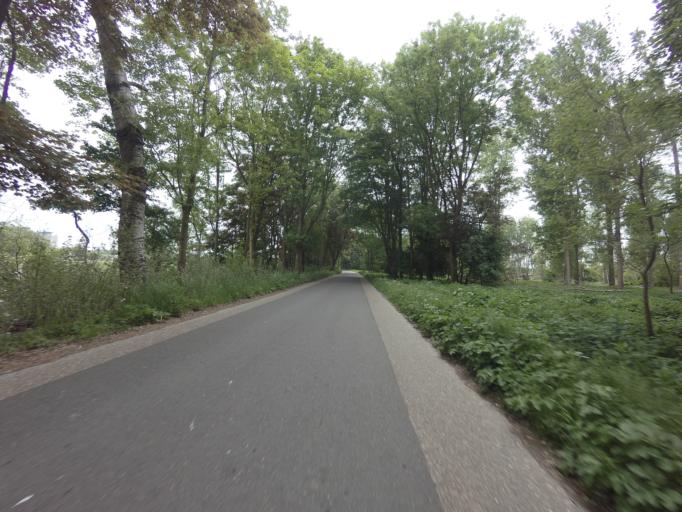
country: NL
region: South Holland
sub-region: Gemeente Vlaardingen
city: Vlaardingen
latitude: 51.9352
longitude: 4.3284
